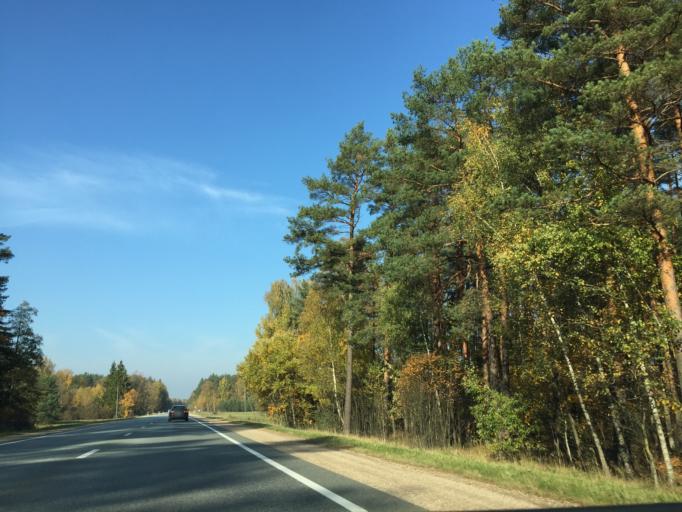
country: LV
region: Babite
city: Pinki
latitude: 56.8909
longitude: 23.9365
